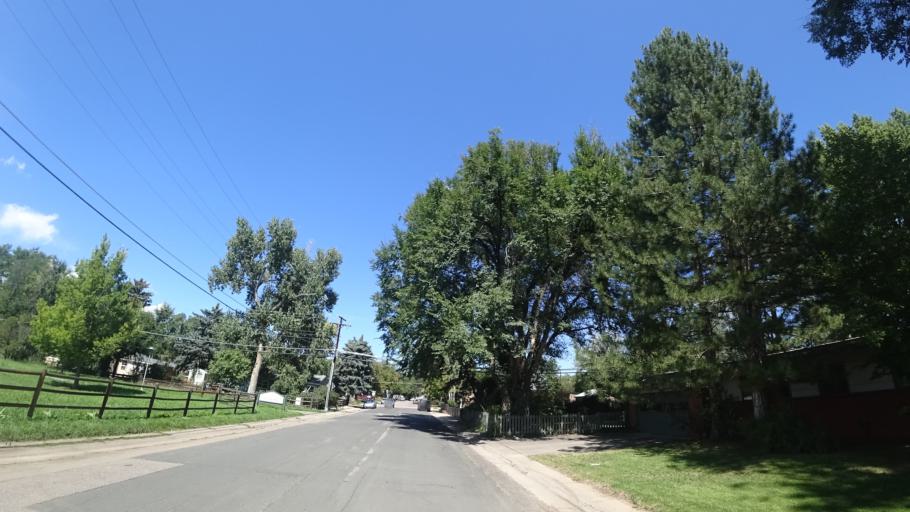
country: US
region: Colorado
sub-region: Arapahoe County
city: Littleton
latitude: 39.6092
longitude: -104.9973
